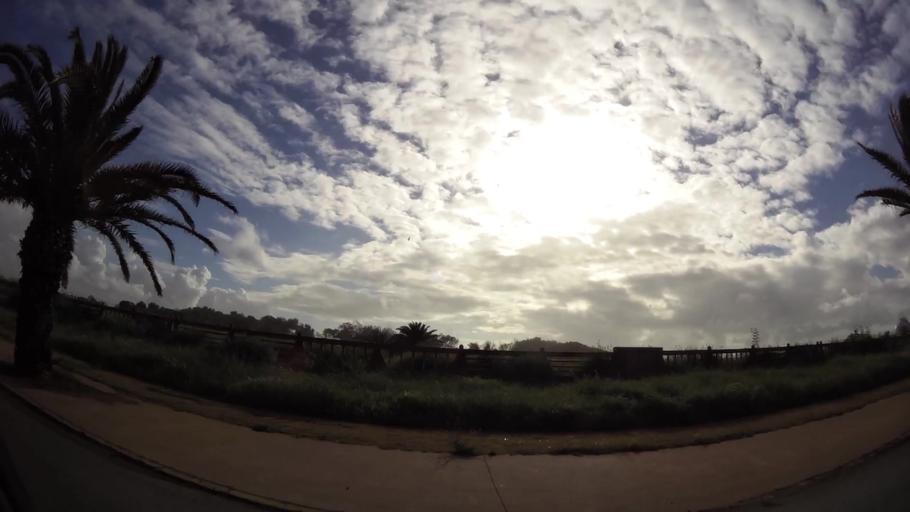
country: MA
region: Grand Casablanca
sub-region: Mohammedia
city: Mohammedia
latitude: 33.7060
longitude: -7.4014
